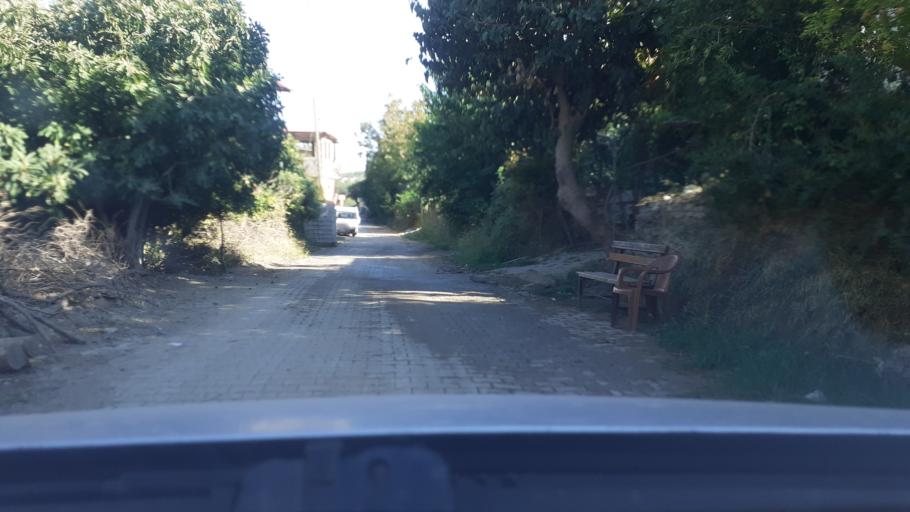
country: TR
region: Hatay
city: Kirikhan
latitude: 36.4880
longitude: 36.3008
